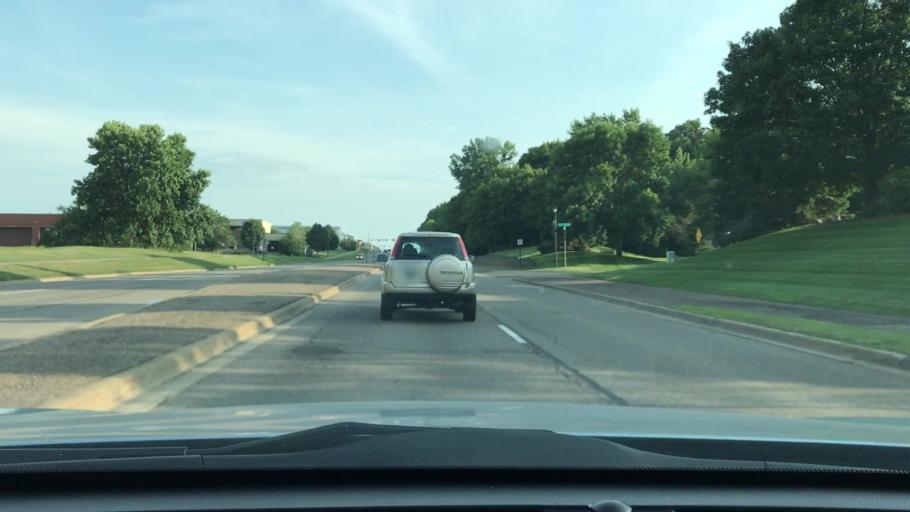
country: US
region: Minnesota
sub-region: Hennepin County
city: Plymouth
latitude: 45.0262
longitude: -93.4818
